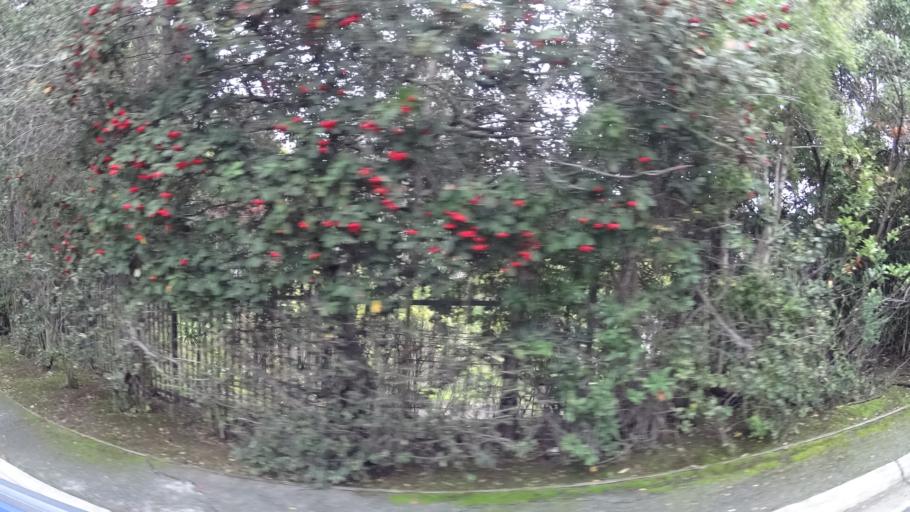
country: US
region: California
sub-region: San Mateo County
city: Burlingame
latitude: 37.5644
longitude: -122.3565
